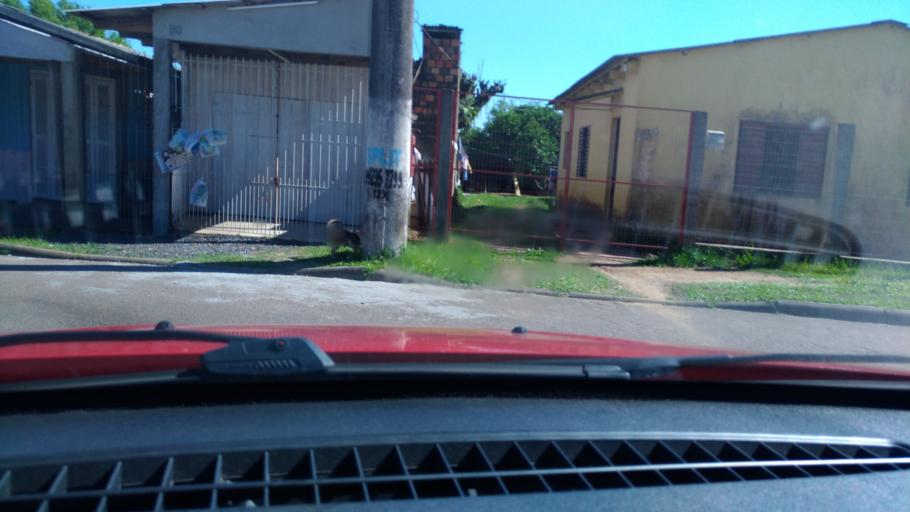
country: BR
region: Rio Grande do Sul
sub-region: Cachoeirinha
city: Cachoeirinha
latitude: -30.0349
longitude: -51.1273
